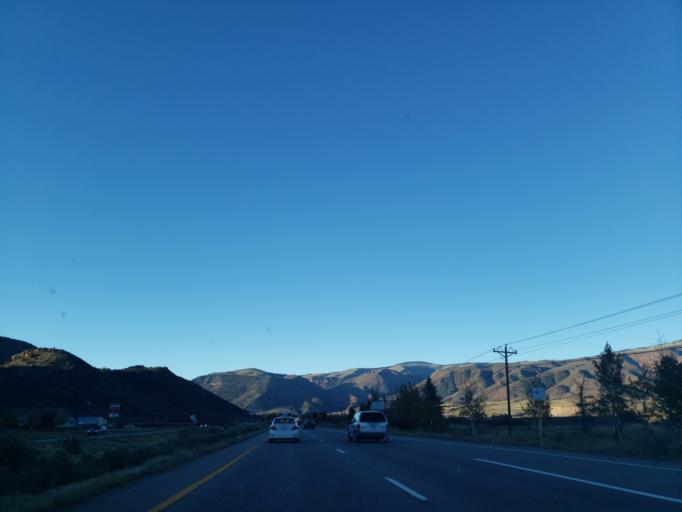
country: US
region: Colorado
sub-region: Pitkin County
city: Snowmass Village
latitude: 39.2544
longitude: -106.8854
